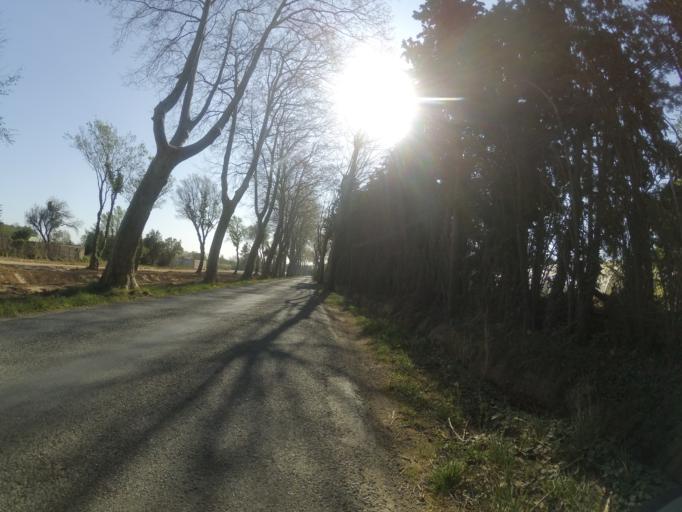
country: FR
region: Languedoc-Roussillon
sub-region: Departement des Pyrenees-Orientales
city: Thuir
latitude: 42.6402
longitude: 2.7465
